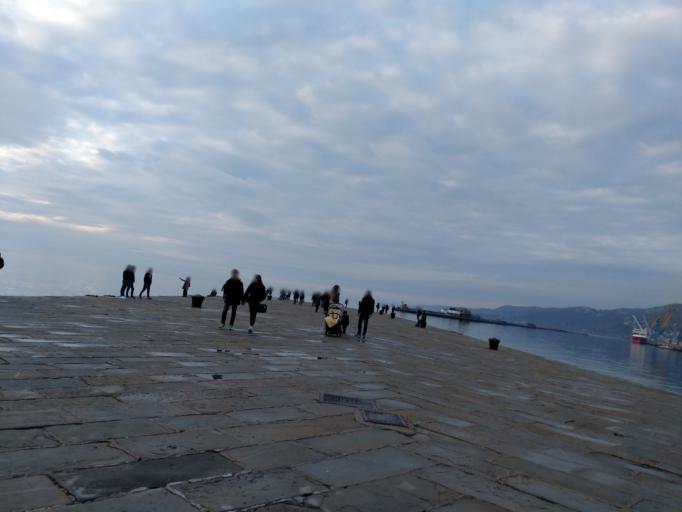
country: IT
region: Friuli Venezia Giulia
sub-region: Provincia di Trieste
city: Trieste
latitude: 45.6522
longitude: 13.7662
